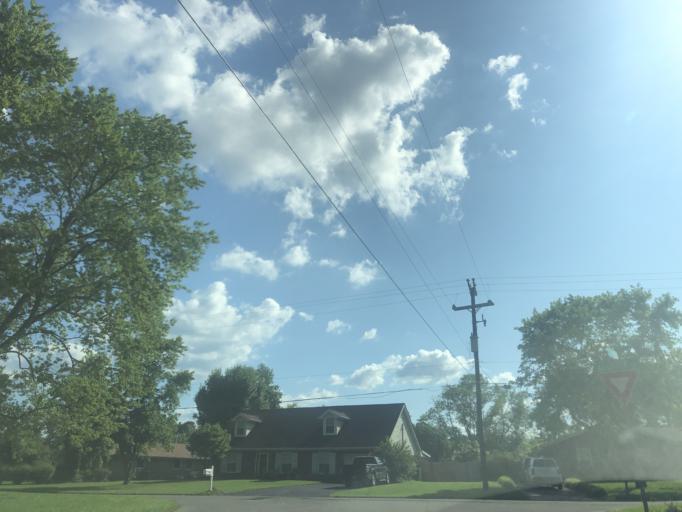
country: US
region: Tennessee
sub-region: Wilson County
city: Green Hill
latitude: 36.2089
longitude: -86.5936
